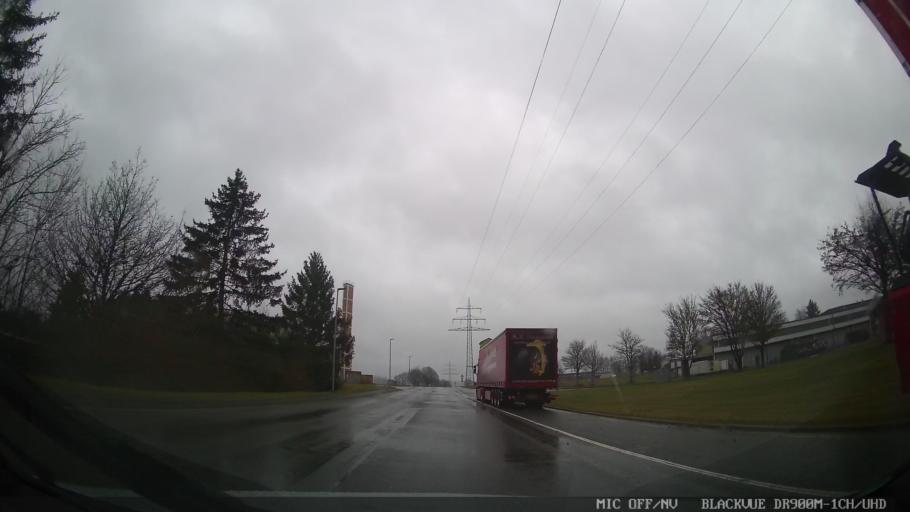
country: DE
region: Rheinland-Pfalz
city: Idar-Oberstein
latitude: 49.7126
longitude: 7.2955
